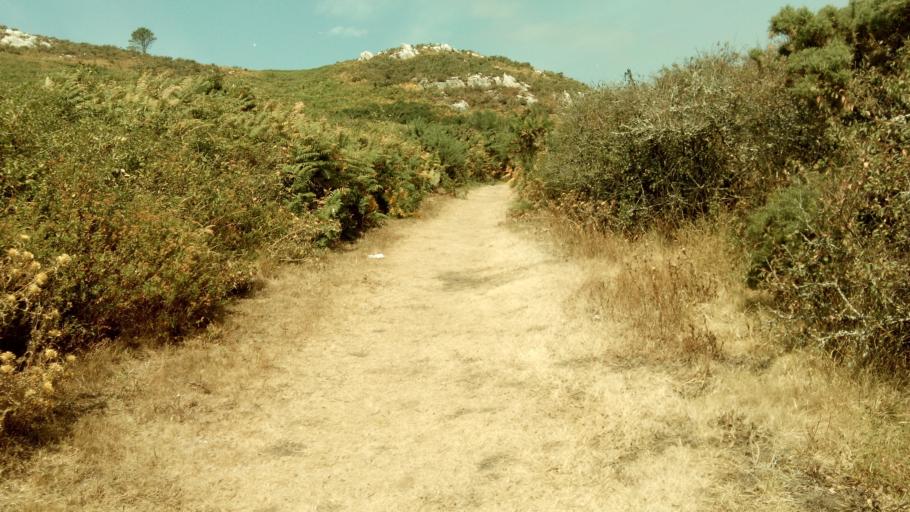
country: ES
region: Galicia
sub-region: Provincia de Pontevedra
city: Sanxenxo
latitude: 42.3796
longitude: -8.9300
